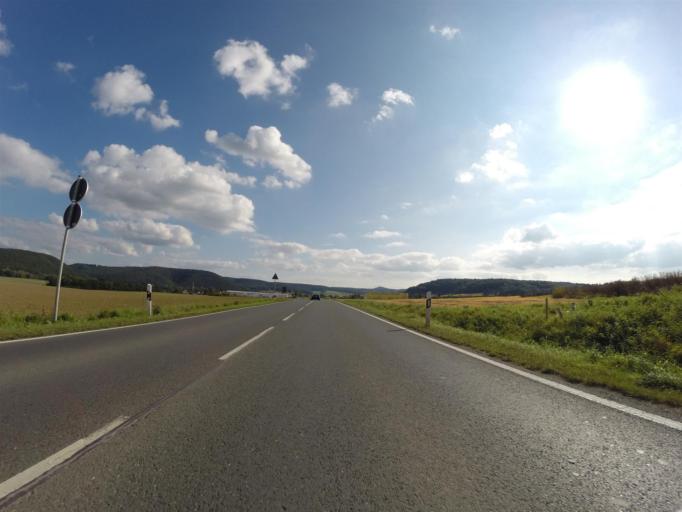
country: DE
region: Thuringia
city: Rothenstein
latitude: 50.8591
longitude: 11.5994
